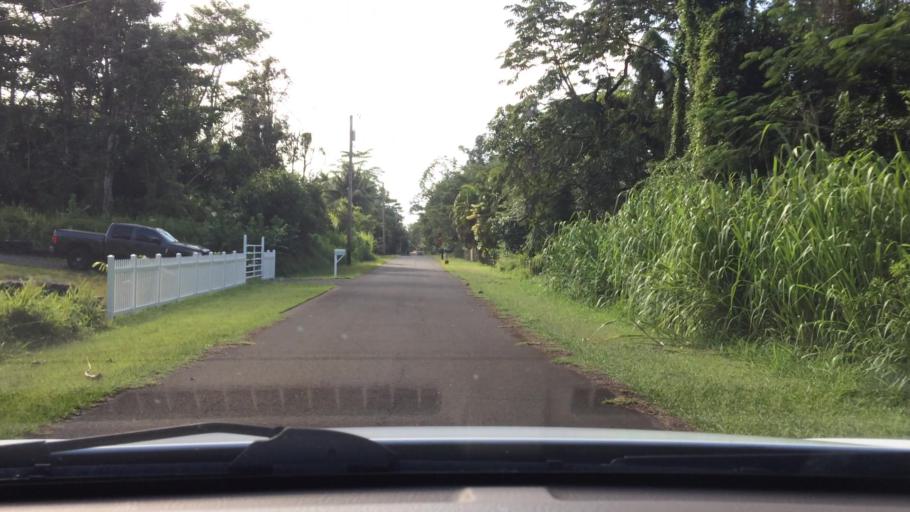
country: US
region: Hawaii
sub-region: Hawaii County
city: Hawaiian Beaches
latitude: 19.5437
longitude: -154.8981
